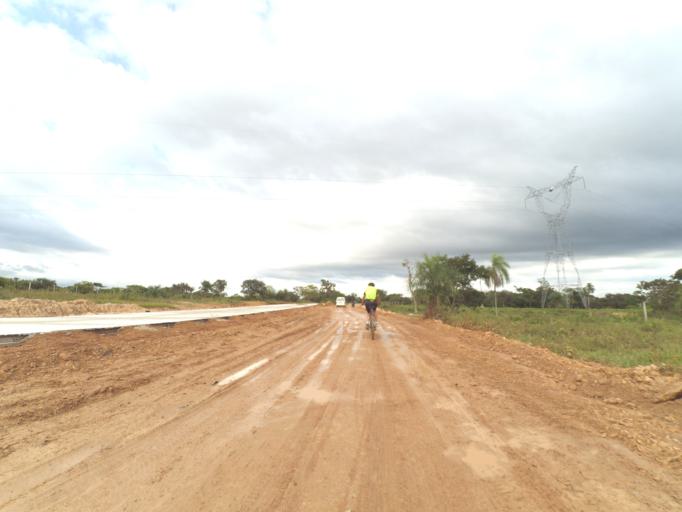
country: BO
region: Santa Cruz
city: Santa Cruz de la Sierra
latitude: -17.7120
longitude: -63.2738
